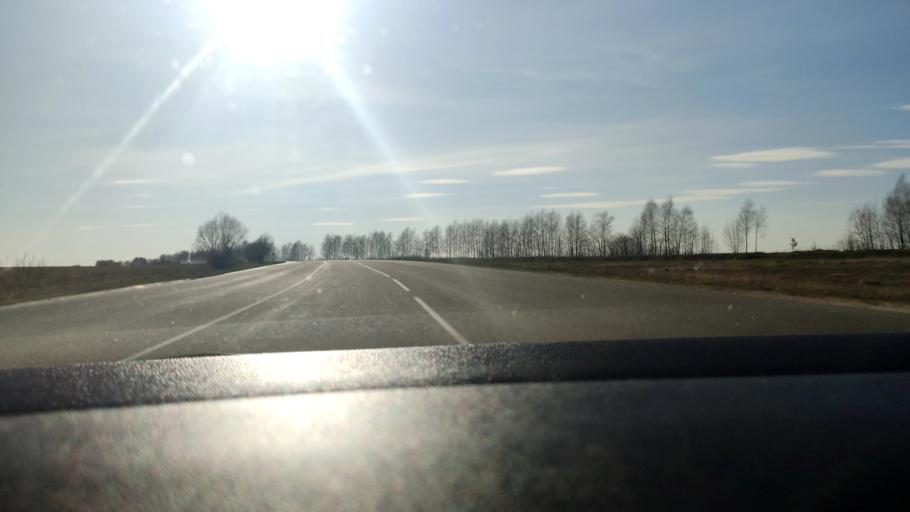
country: RU
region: Voronezj
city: Kolodeznyy
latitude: 51.3290
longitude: 39.1370
